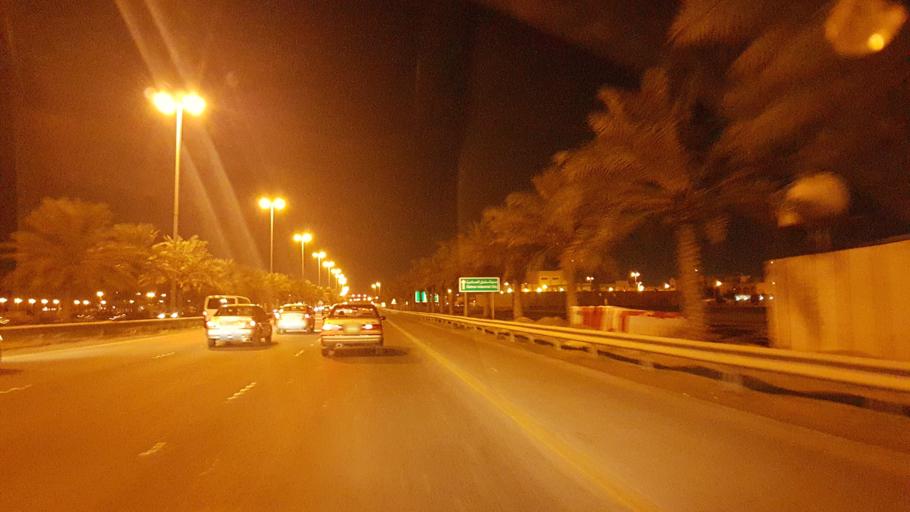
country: BH
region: Muharraq
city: Al Hadd
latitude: 26.2492
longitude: 50.6590
